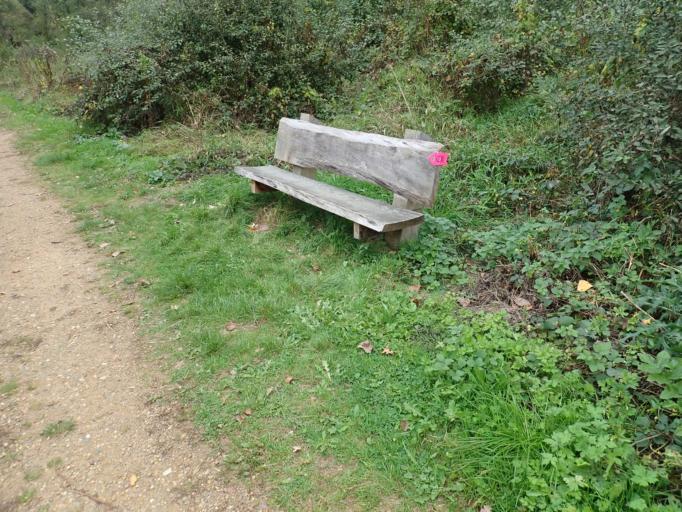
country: BE
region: Flanders
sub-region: Provincie Antwerpen
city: Rumst
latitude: 51.0574
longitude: 4.3977
